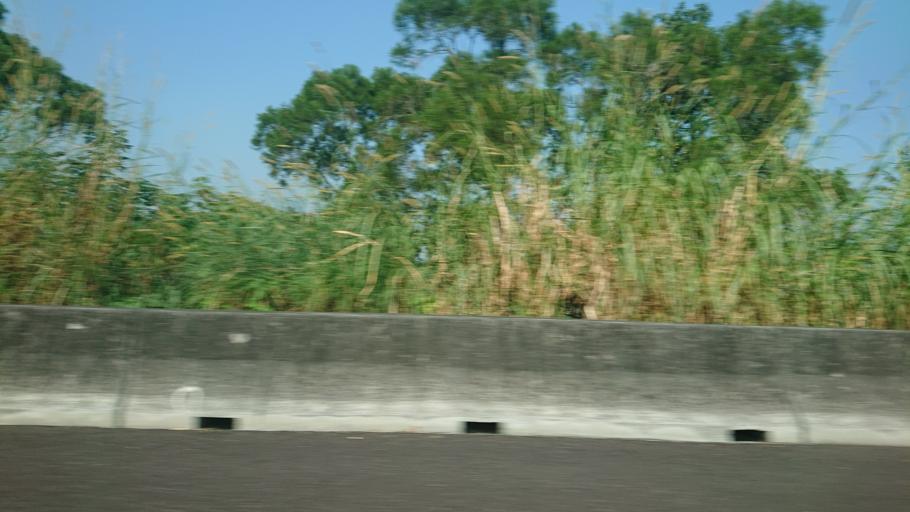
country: TW
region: Taiwan
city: Lugu
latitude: 23.8168
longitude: 120.7018
